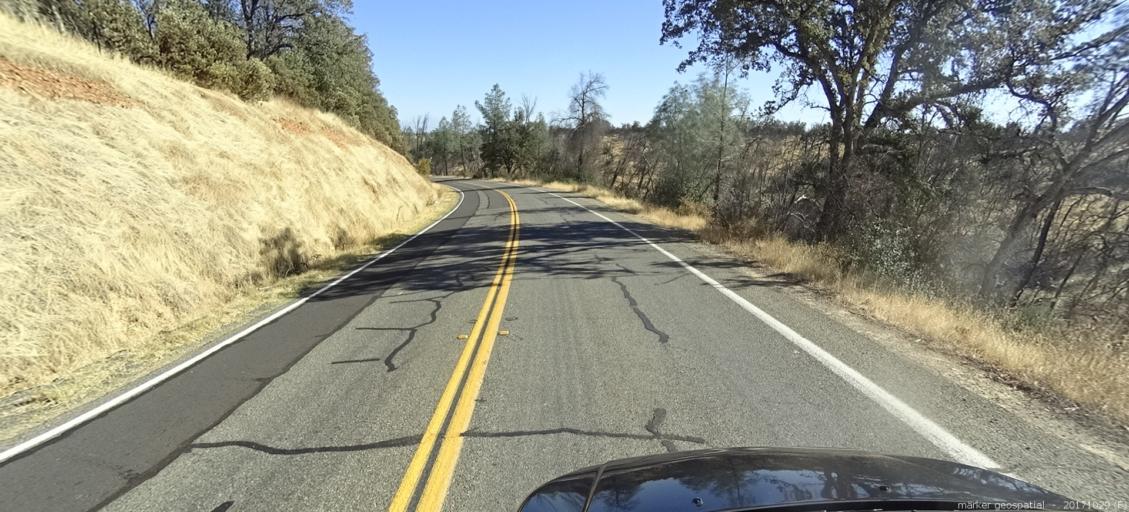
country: US
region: California
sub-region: Shasta County
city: Shasta
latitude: 40.4899
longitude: -122.5342
